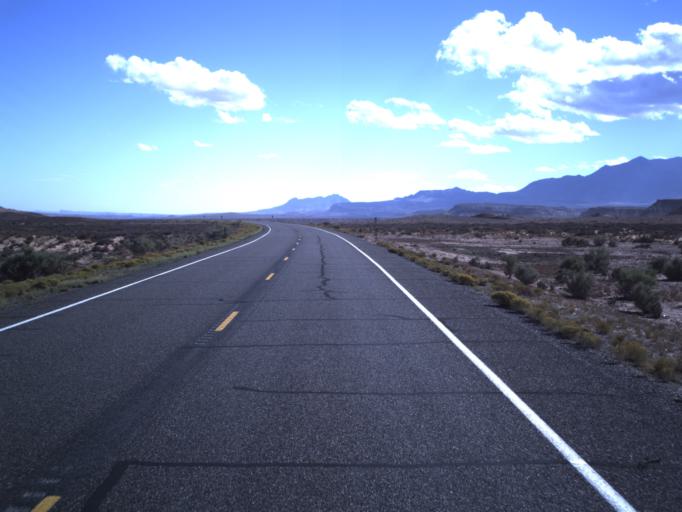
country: US
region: Utah
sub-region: Wayne County
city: Loa
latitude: 38.1030
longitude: -110.6238
